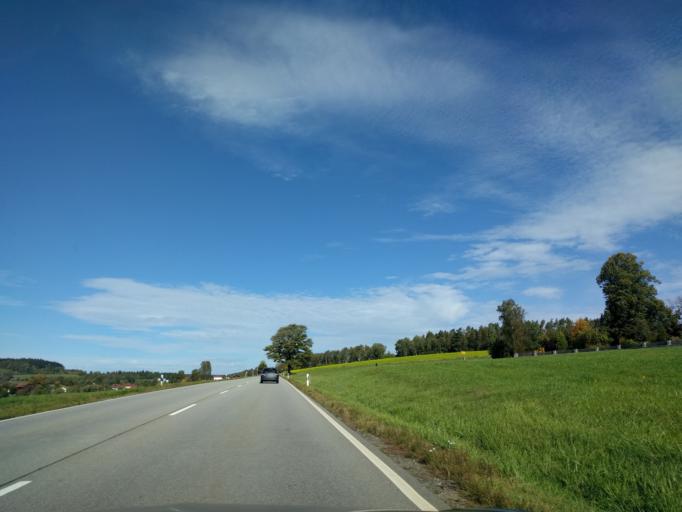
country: DE
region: Bavaria
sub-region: Lower Bavaria
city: Patersdorf
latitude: 49.0175
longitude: 12.9782
